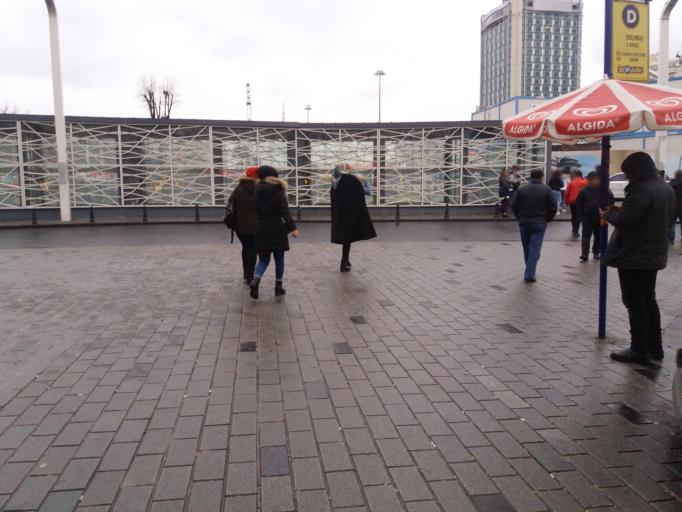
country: TR
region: Istanbul
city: Eminoenue
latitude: 41.0378
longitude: 28.9841
